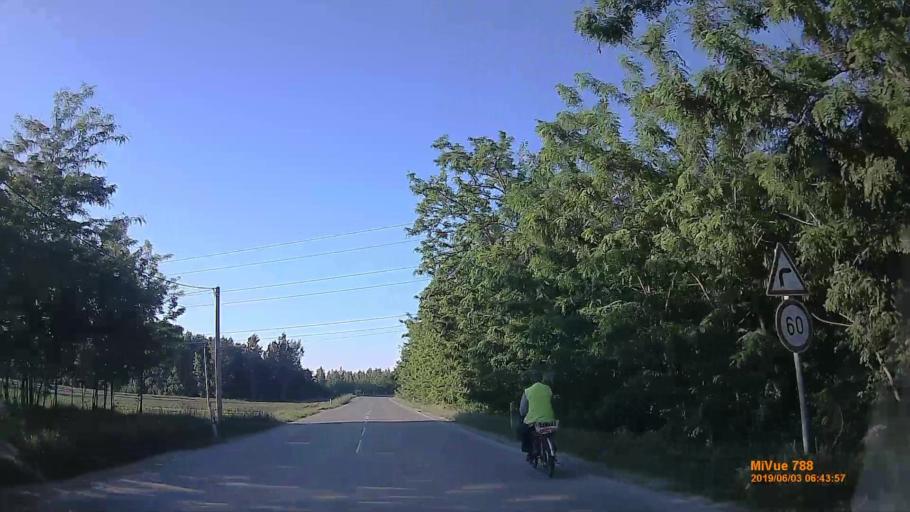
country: HU
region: Pest
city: Bugyi
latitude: 47.2493
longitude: 19.1283
